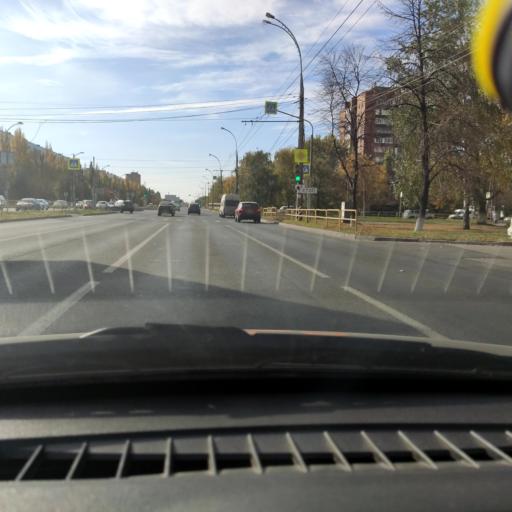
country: RU
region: Samara
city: Tol'yatti
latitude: 53.5145
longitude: 49.2936
